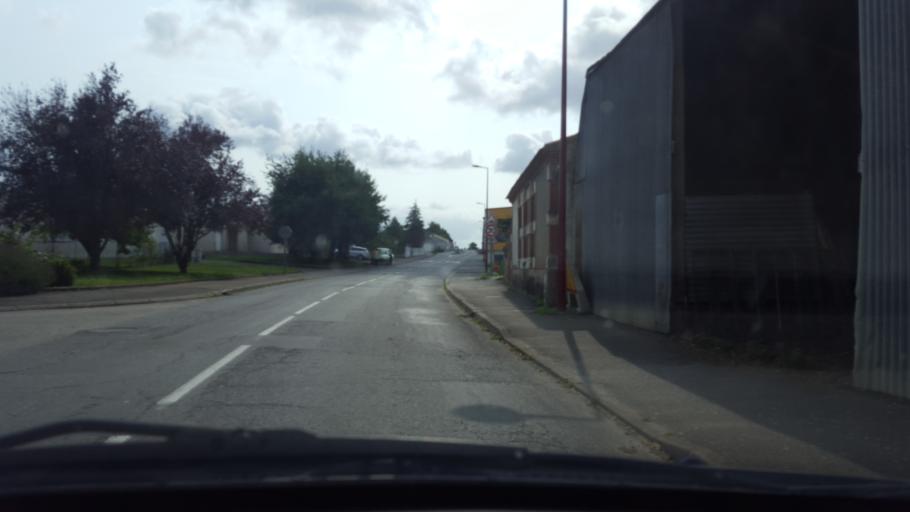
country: FR
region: Pays de la Loire
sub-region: Departement de la Loire-Atlantique
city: Saint-Meme-le-Tenu
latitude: 47.0195
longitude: -1.7943
